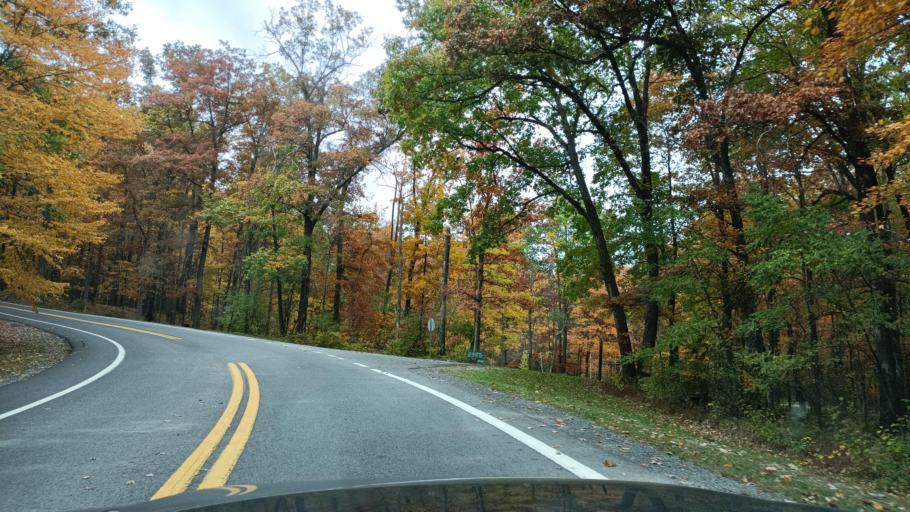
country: US
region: West Virginia
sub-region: Monongalia County
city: Cheat Lake
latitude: 39.6563
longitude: -79.7853
